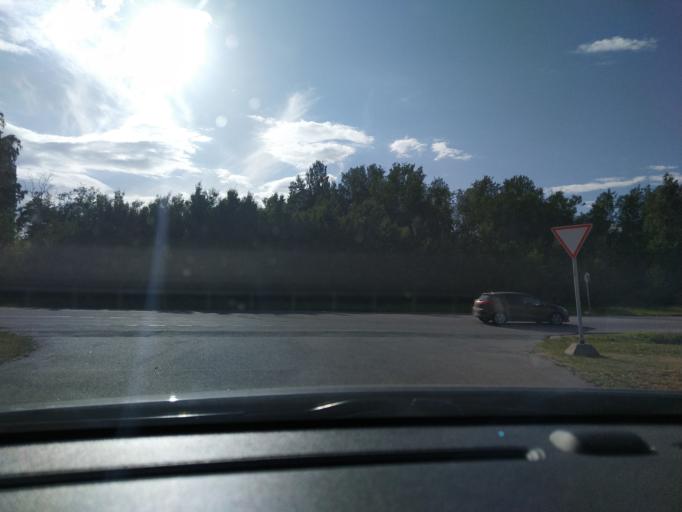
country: RU
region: St.-Petersburg
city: Gorelovo
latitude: 59.7808
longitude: 30.1703
